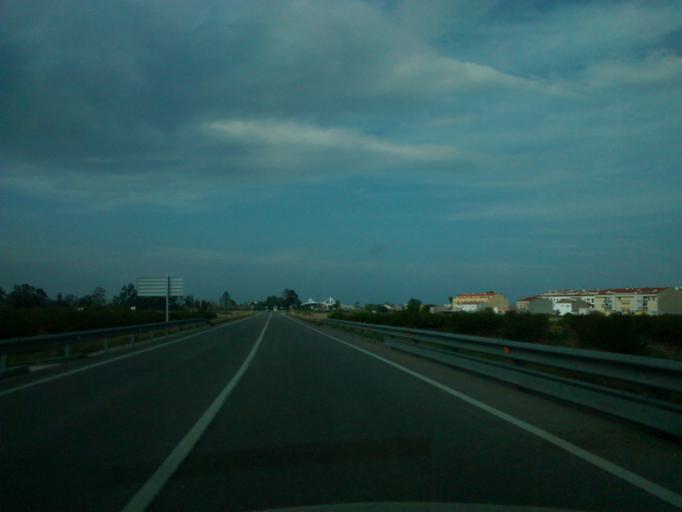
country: ES
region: Catalonia
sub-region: Provincia de Tarragona
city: Deltebre
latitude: 40.7062
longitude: 0.7118
